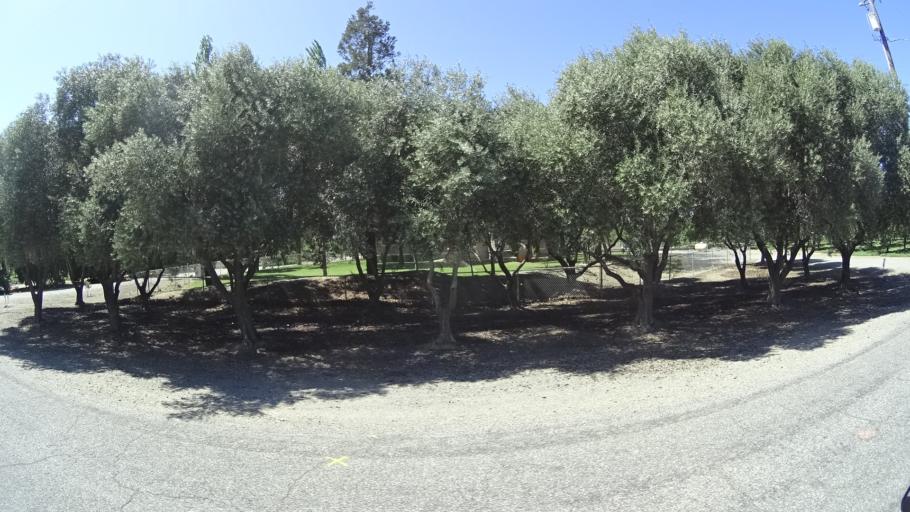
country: US
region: California
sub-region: Glenn County
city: Orland
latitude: 39.7380
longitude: -122.1594
